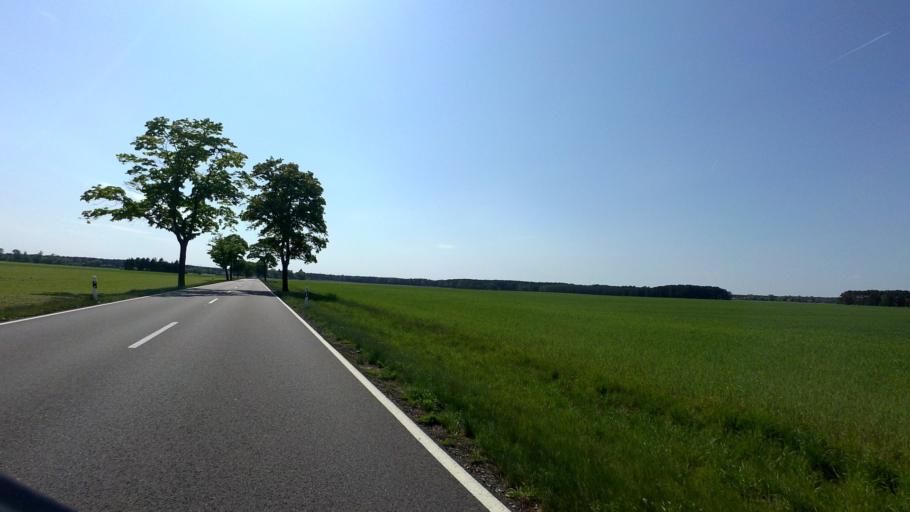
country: DE
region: Brandenburg
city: Neu Zauche
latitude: 52.0125
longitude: 14.0622
